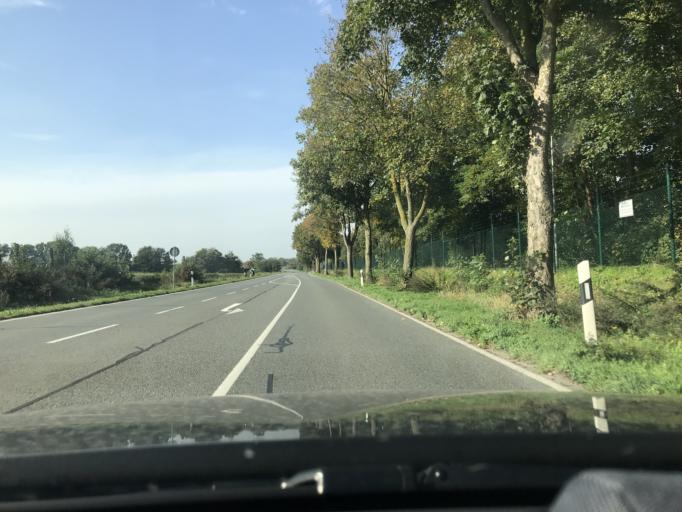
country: DE
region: North Rhine-Westphalia
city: Kalkar
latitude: 51.7322
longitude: 6.2676
